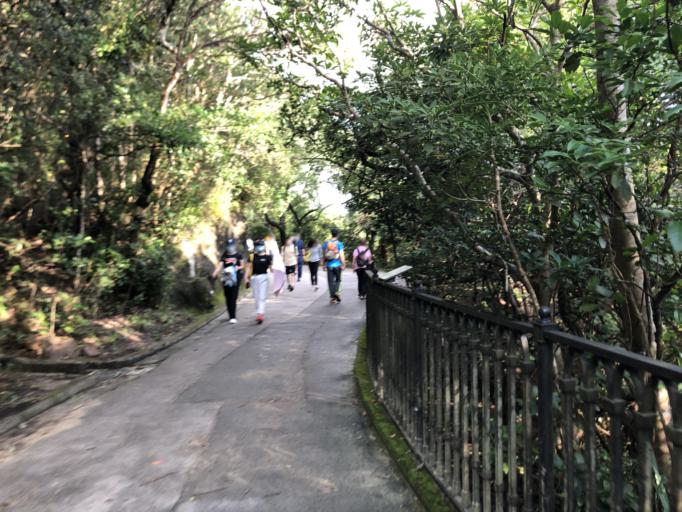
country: HK
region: Central and Western
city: Central
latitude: 22.2724
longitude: 114.1413
